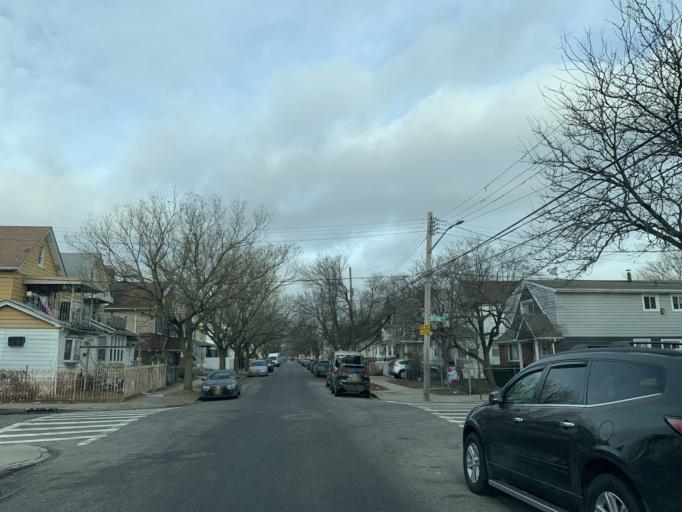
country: US
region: New York
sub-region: Queens County
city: Jamaica
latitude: 40.6899
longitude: -73.8049
